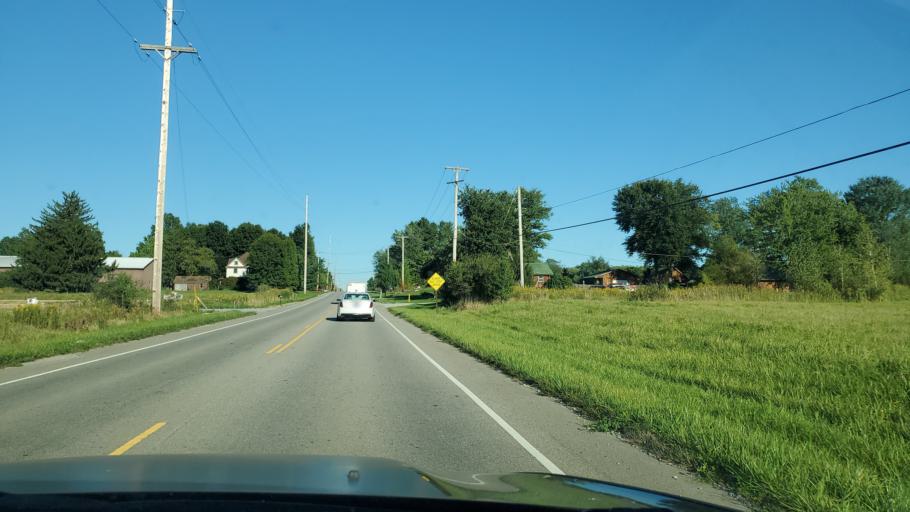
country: US
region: Ohio
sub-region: Mahoning County
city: Boardman
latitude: 40.9880
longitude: -80.6862
